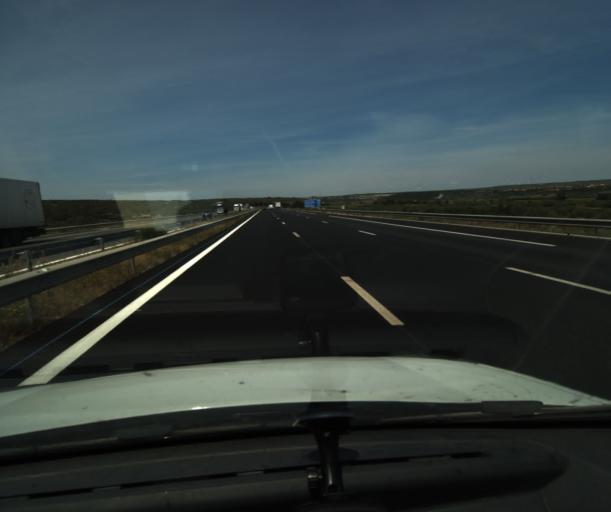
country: FR
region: Languedoc-Roussillon
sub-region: Departement de l'Aude
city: Sigean
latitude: 42.9586
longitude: 2.9698
